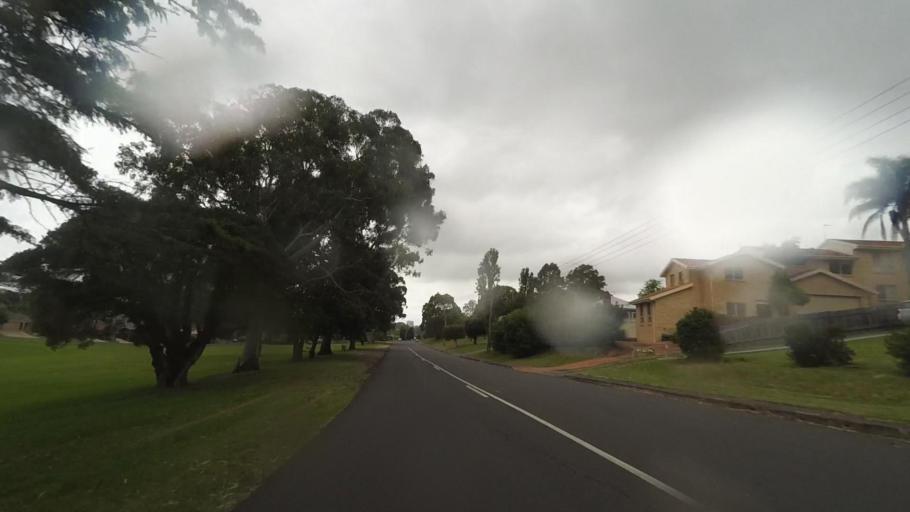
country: AU
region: New South Wales
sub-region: Wollongong
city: Cordeaux Heights
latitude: -34.4481
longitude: 150.8401
